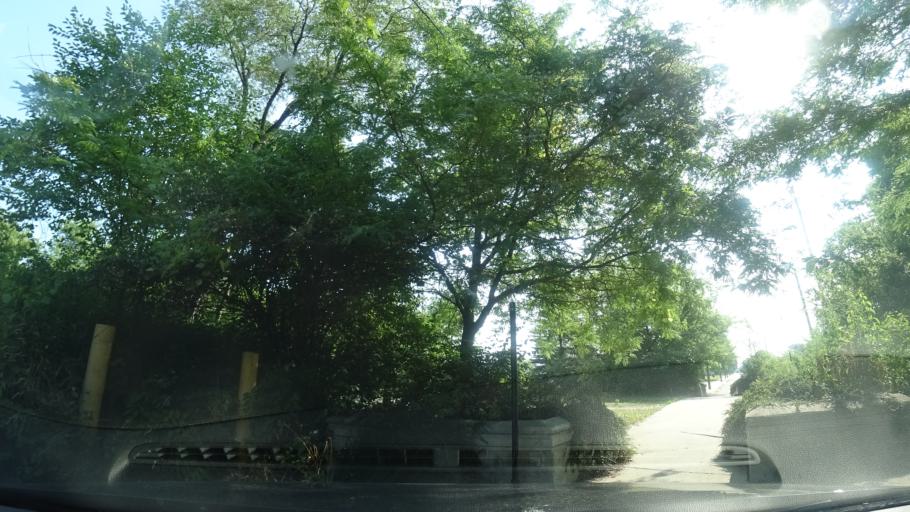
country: US
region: Illinois
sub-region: Cook County
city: Lincolnwood
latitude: 41.9828
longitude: -87.7376
